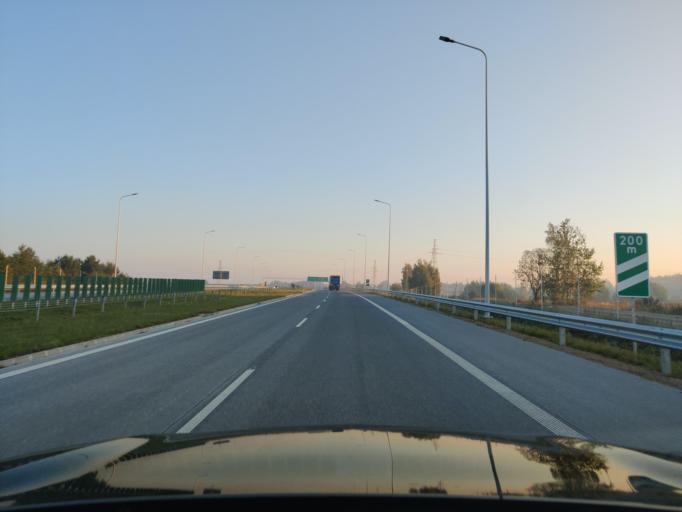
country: PL
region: Masovian Voivodeship
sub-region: Powiat mlawski
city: Mlawa
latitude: 53.0924
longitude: 20.4098
